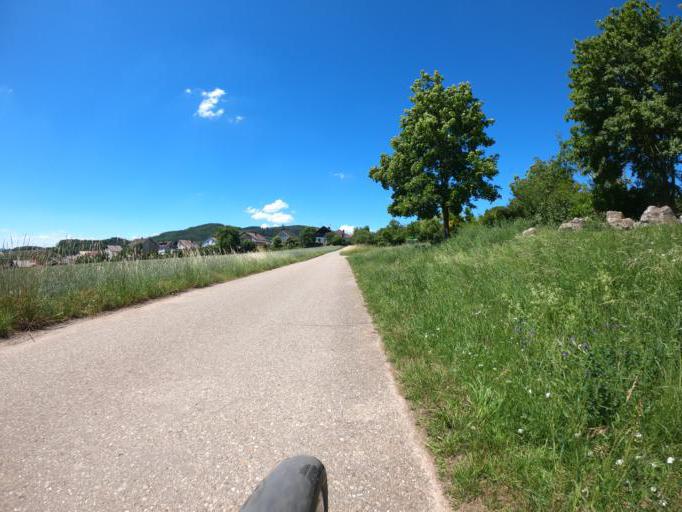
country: DE
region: Baden-Wuerttemberg
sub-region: Regierungsbezirk Stuttgart
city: Sersheim
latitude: 49.0035
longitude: 9.0212
